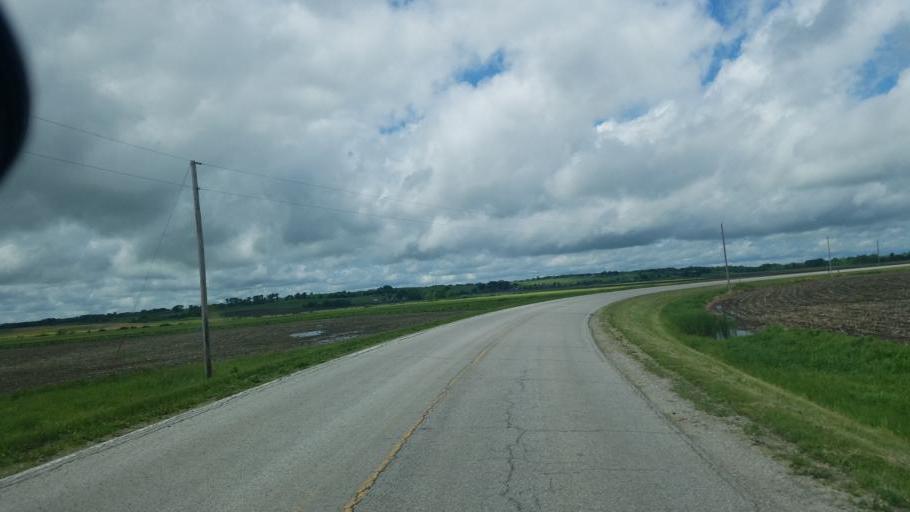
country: US
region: Iowa
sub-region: Decatur County
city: Leon
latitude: 40.6072
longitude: -93.7938
